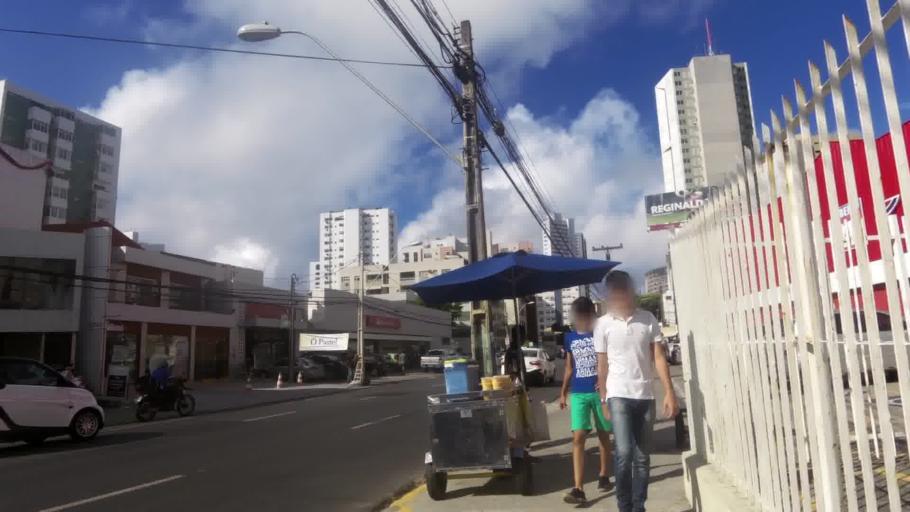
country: BR
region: Pernambuco
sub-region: Recife
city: Recife
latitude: -8.1268
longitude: -34.8997
